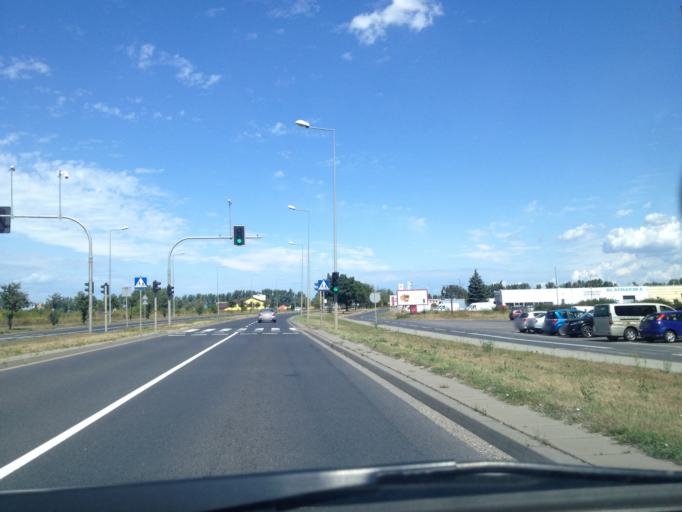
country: PL
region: Lower Silesian Voivodeship
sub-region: Legnica
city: Legnica
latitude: 51.1711
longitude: 16.1720
